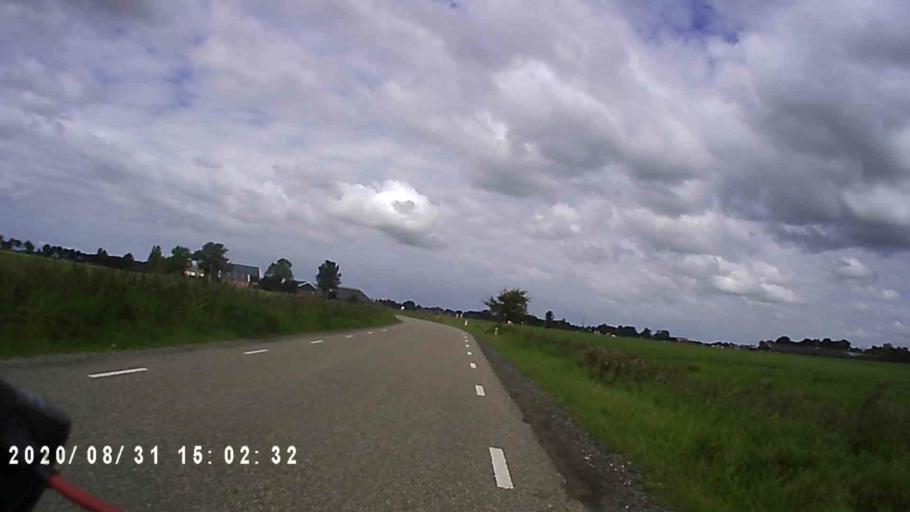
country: NL
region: Groningen
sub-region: Gemeente Zuidhorn
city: Oldehove
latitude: 53.2907
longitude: 6.3923
